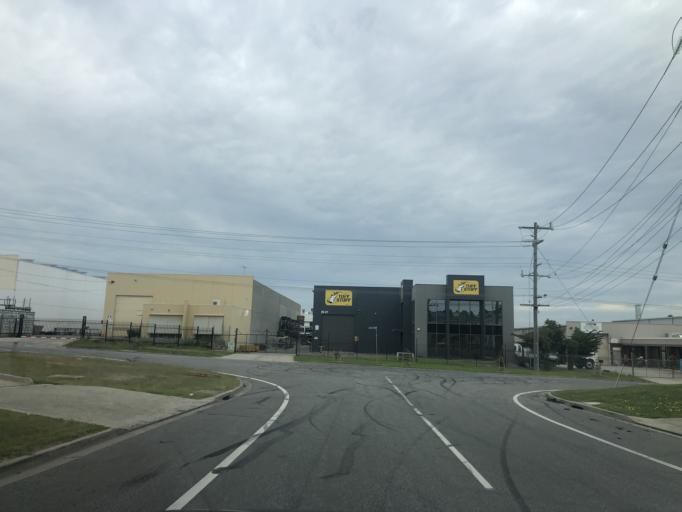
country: AU
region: Victoria
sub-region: Casey
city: Hallam
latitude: -38.0138
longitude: 145.2665
